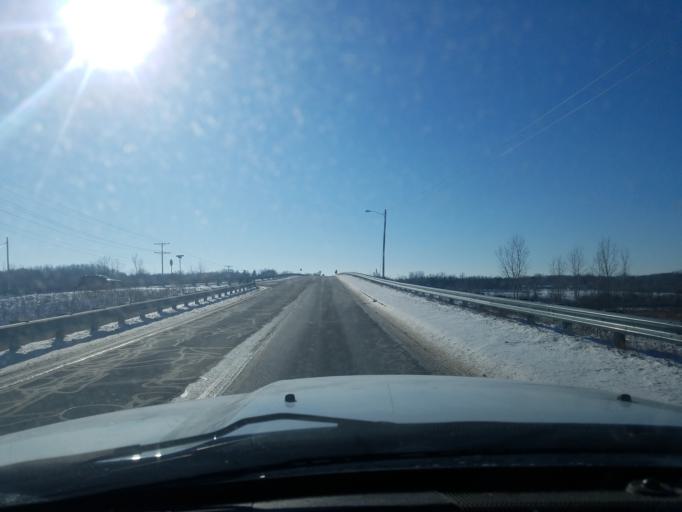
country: US
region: Indiana
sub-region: Noble County
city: Kendallville
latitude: 41.4424
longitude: -85.2318
